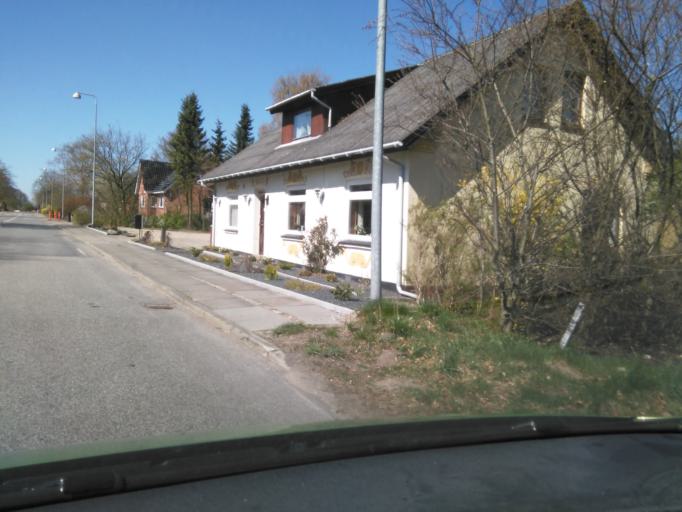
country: DK
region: South Denmark
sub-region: Billund Kommune
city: Grindsted
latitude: 55.6915
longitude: 8.9203
